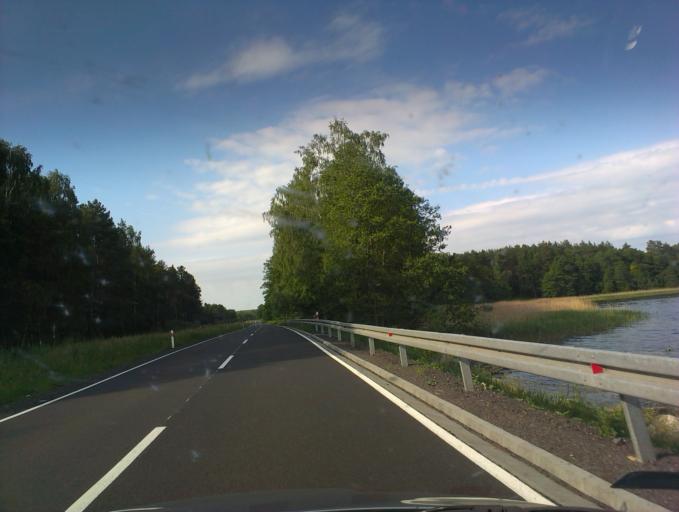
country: PL
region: West Pomeranian Voivodeship
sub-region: Powiat szczecinecki
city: Lubowo
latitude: 53.6093
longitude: 16.4448
